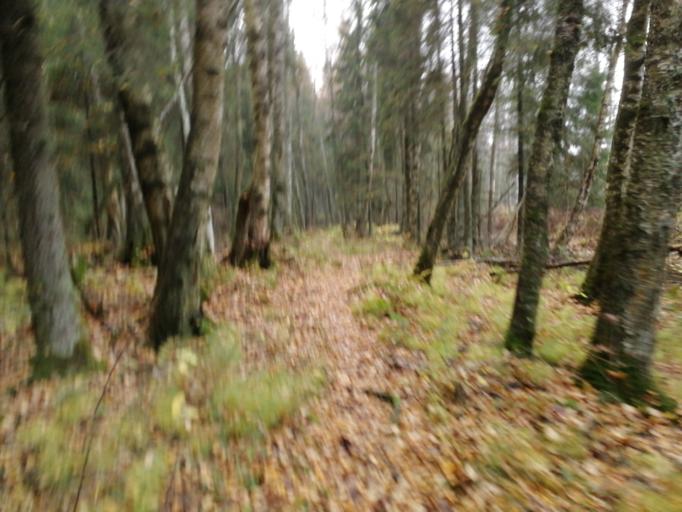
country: FI
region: Pirkanmaa
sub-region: Tampere
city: Tampere
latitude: 61.4486
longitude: 23.8913
